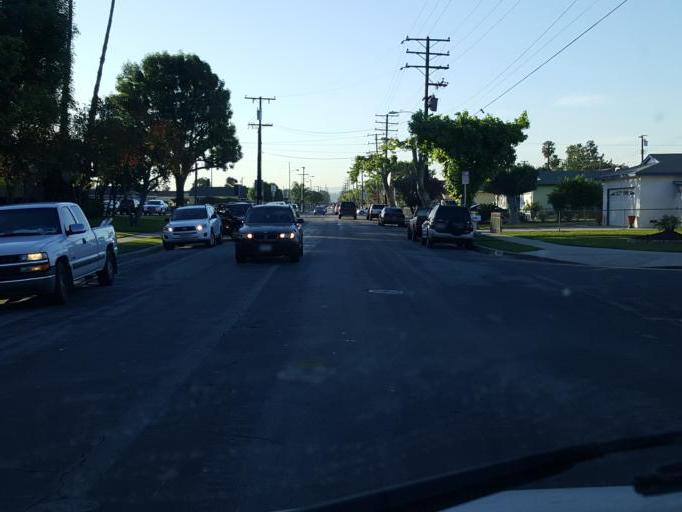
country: US
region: California
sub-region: Los Angeles County
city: West Puente Valley
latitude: 34.0536
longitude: -117.9651
